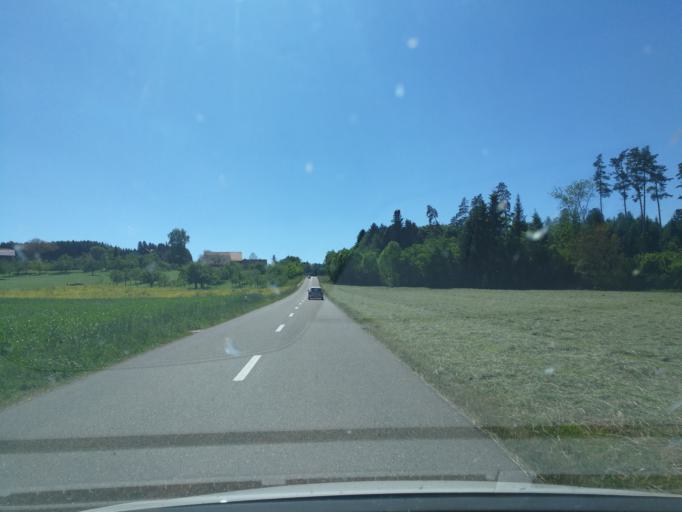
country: CH
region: Thurgau
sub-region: Weinfelden District
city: Sulgen
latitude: 47.5075
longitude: 9.1571
